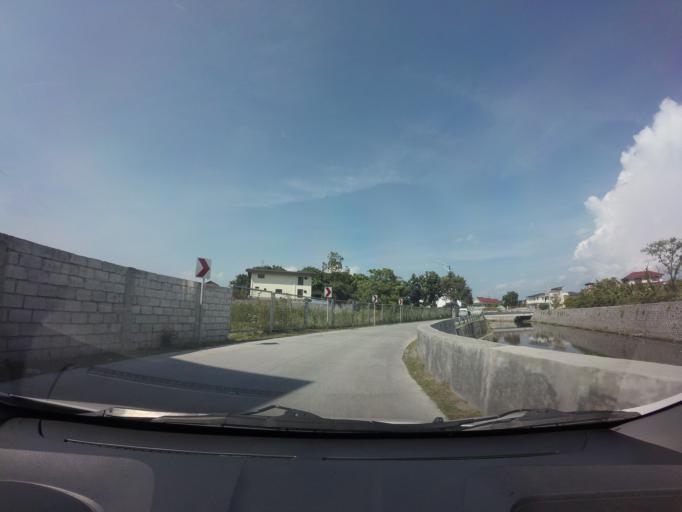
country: PH
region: Calabarzon
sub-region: Province of Rizal
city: Las Pinas
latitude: 14.4700
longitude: 120.9847
